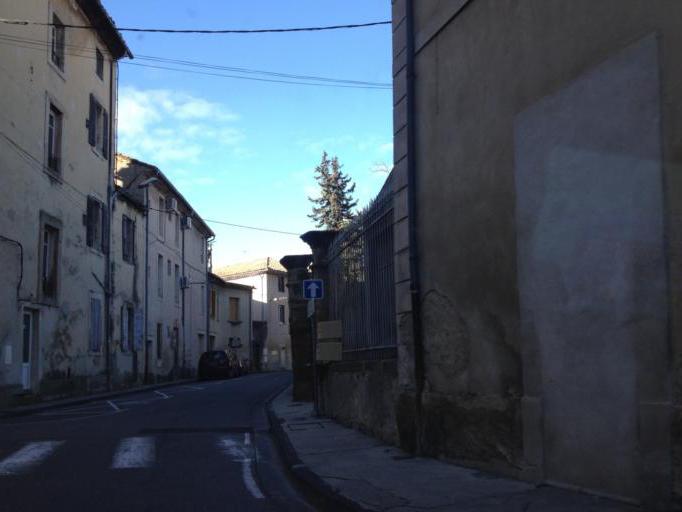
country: FR
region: Provence-Alpes-Cote d'Azur
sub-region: Departement du Vaucluse
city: Orange
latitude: 44.1386
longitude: 4.8090
